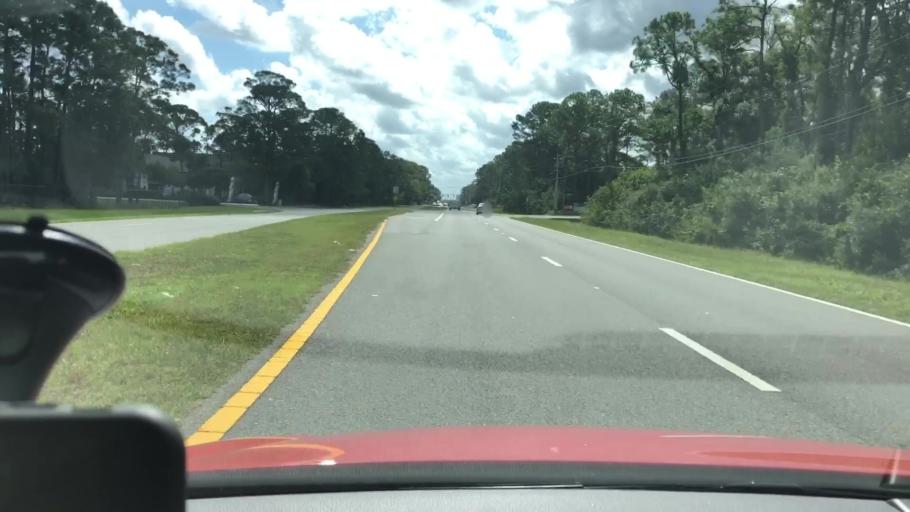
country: US
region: Florida
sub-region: Volusia County
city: Daytona Beach
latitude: 29.2050
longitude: -81.0731
